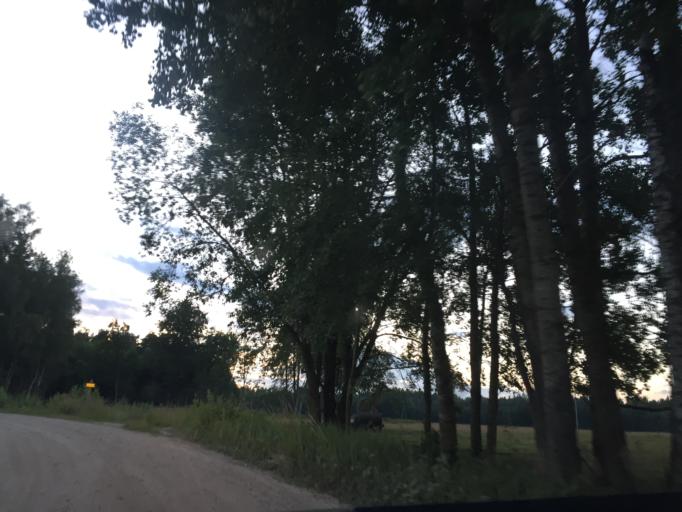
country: LV
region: Koknese
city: Koknese
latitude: 56.6208
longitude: 25.4921
